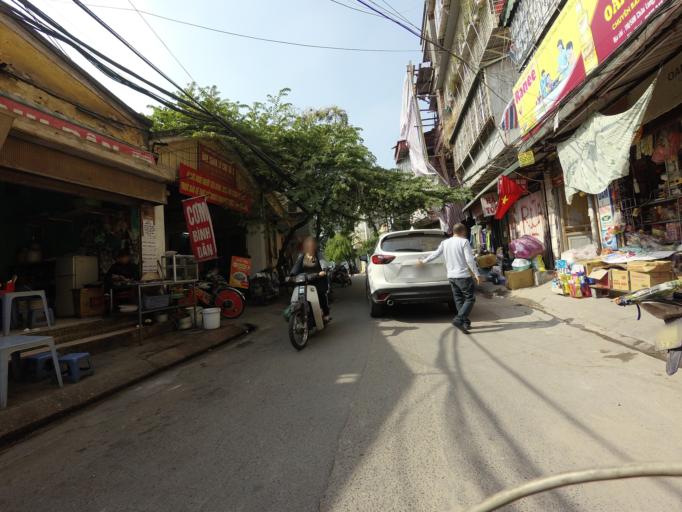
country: VN
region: Ha Noi
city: Hoan Kiem
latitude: 21.0442
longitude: 105.8422
